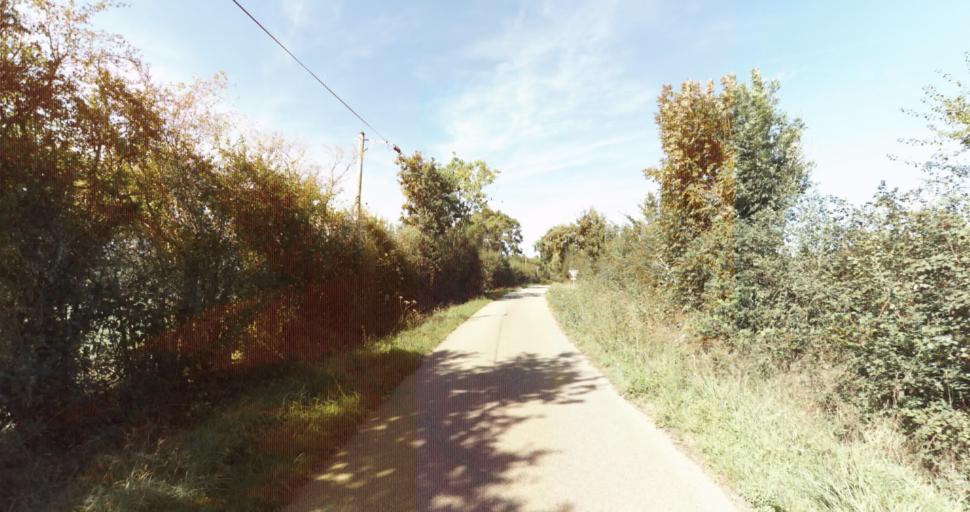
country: FR
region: Lower Normandy
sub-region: Departement de l'Orne
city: Gace
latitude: 48.7607
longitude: 0.2425
